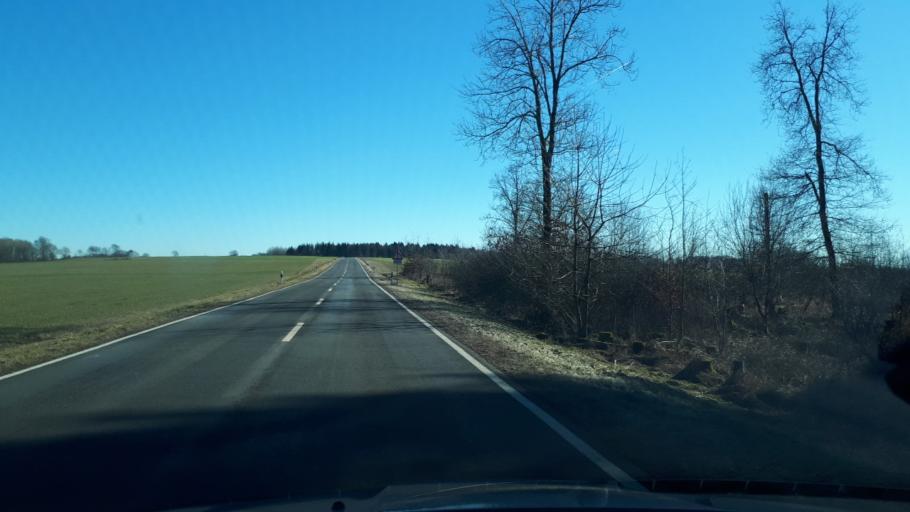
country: DE
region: Rheinland-Pfalz
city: Brockscheid
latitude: 50.1297
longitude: 6.8649
